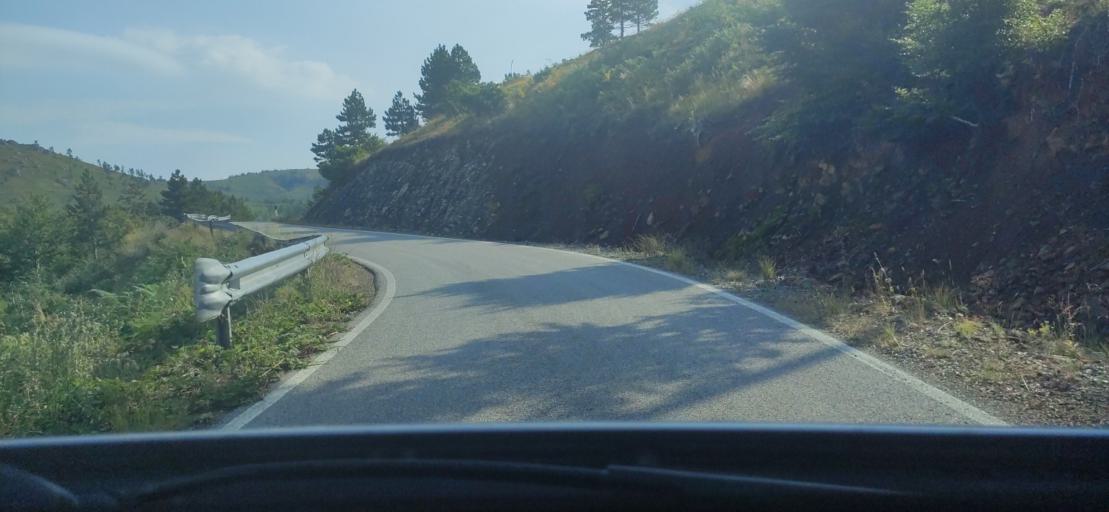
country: AL
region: Shkoder
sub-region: Rrethi i Pukes
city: Iballe
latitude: 42.1719
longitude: 20.0239
